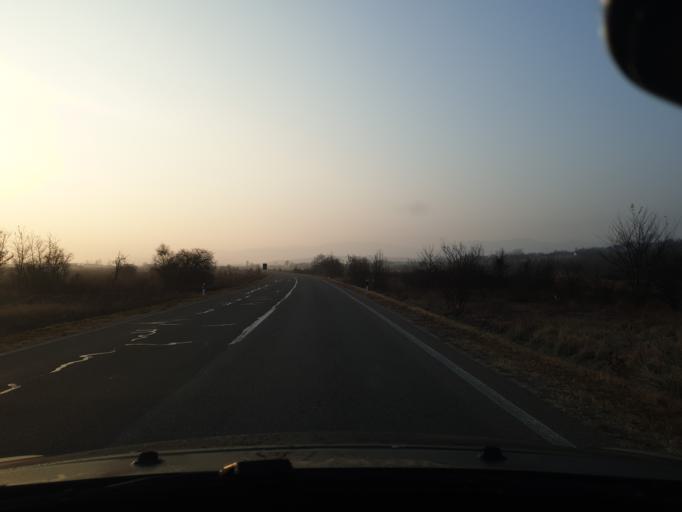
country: RS
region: Central Serbia
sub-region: Jablanicki Okrug
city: Leskovac
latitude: 42.9463
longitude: 21.9922
